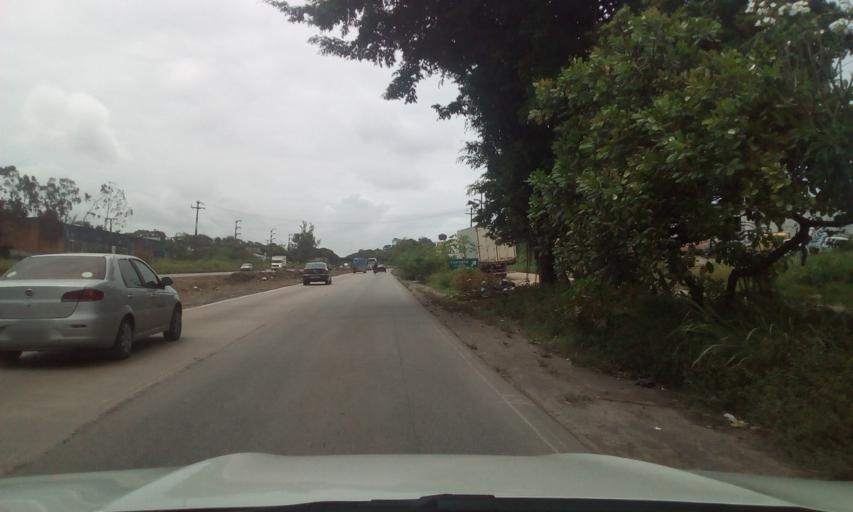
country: BR
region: Pernambuco
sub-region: Abreu E Lima
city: Abreu e Lima
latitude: -7.9323
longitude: -34.9016
